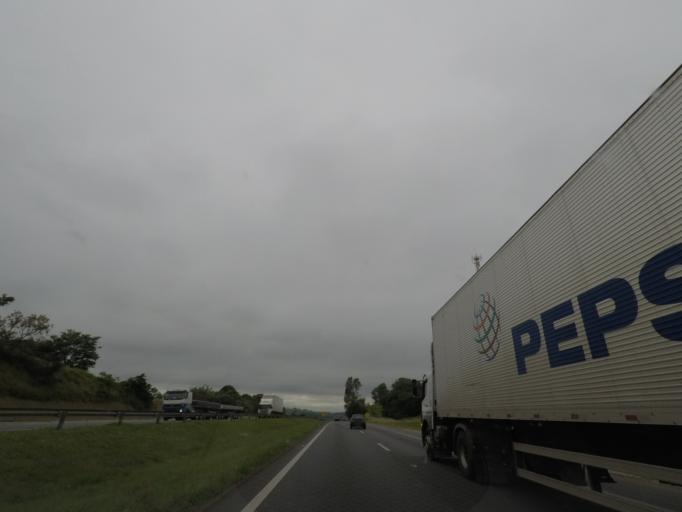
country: BR
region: Sao Paulo
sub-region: Jarinu
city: Jarinu
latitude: -23.0375
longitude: -46.6929
